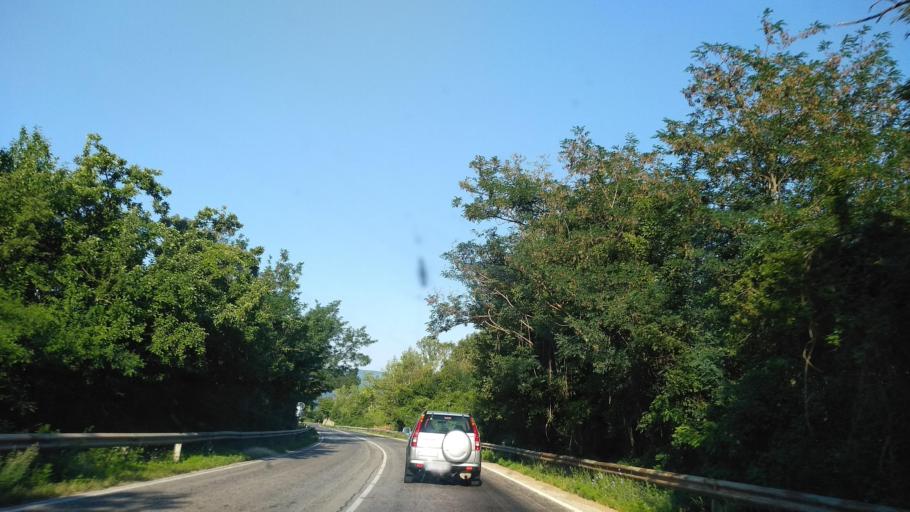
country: BG
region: Lovech
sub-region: Obshtina Lovech
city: Lovech
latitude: 43.0489
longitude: 24.7929
